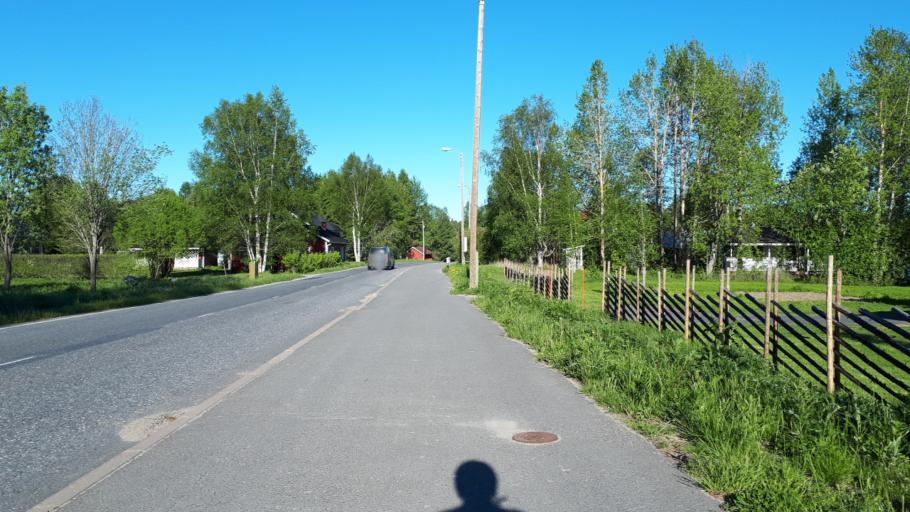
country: FI
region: Northern Ostrobothnia
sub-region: Oulunkaari
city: Ii
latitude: 65.3231
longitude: 25.4496
